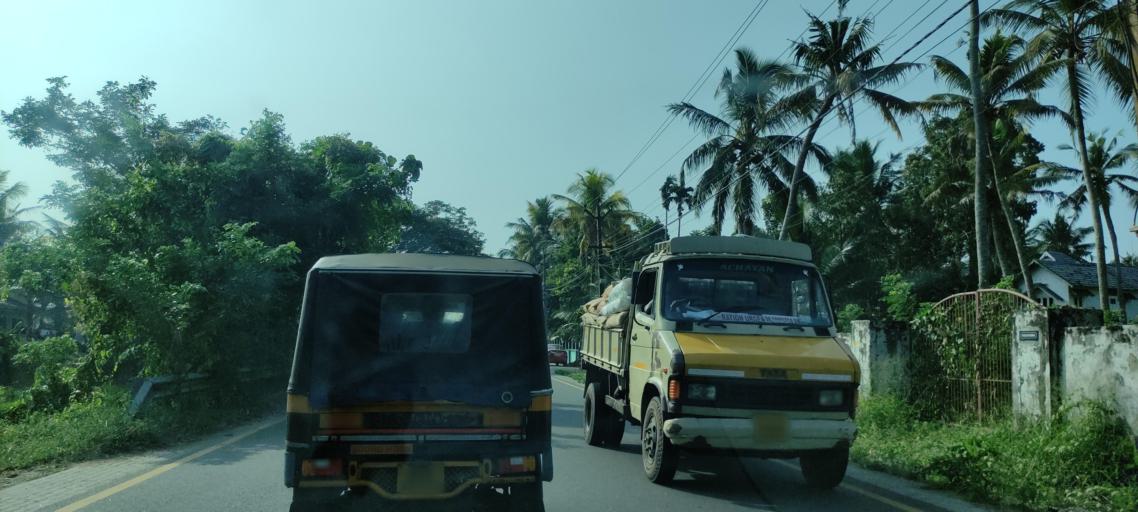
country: IN
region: Kerala
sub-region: Kottayam
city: Changanacheri
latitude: 9.3618
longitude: 76.4665
